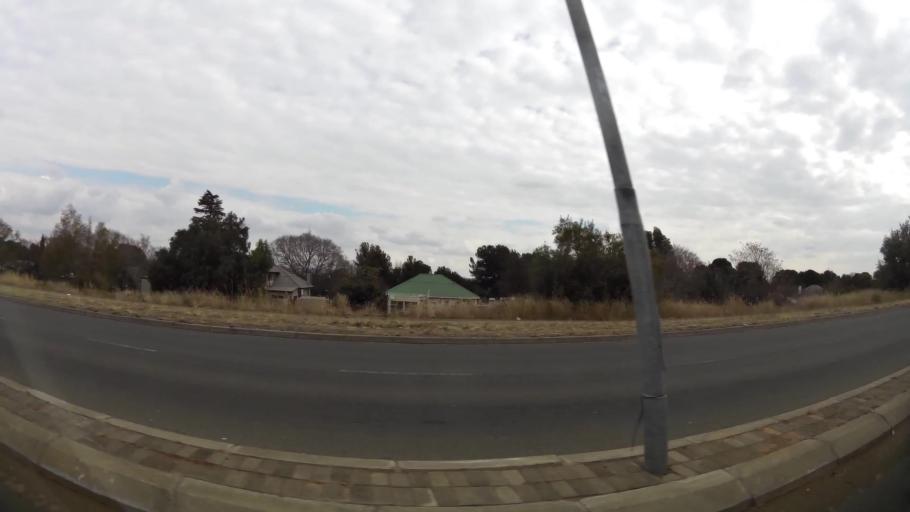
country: ZA
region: Orange Free State
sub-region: Mangaung Metropolitan Municipality
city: Bloemfontein
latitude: -29.1026
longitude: 26.2125
